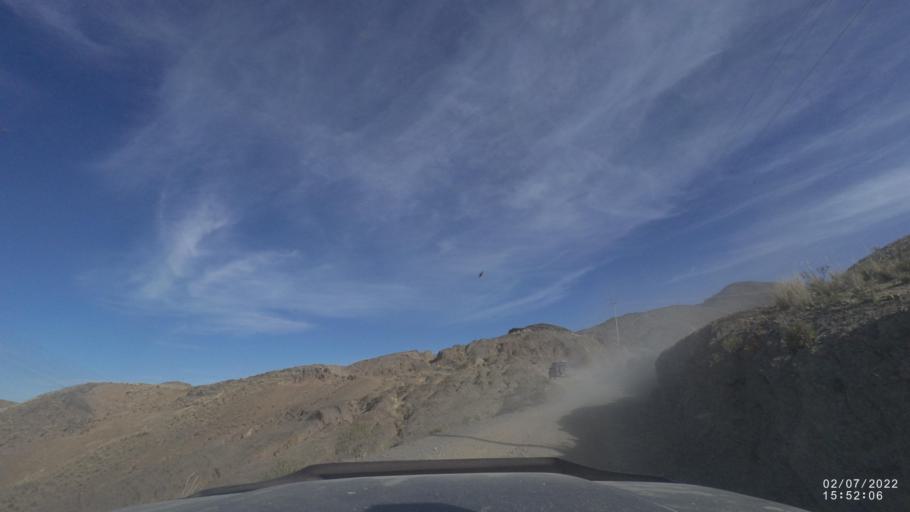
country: BO
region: Cochabamba
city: Irpa Irpa
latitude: -17.9062
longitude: -66.4137
